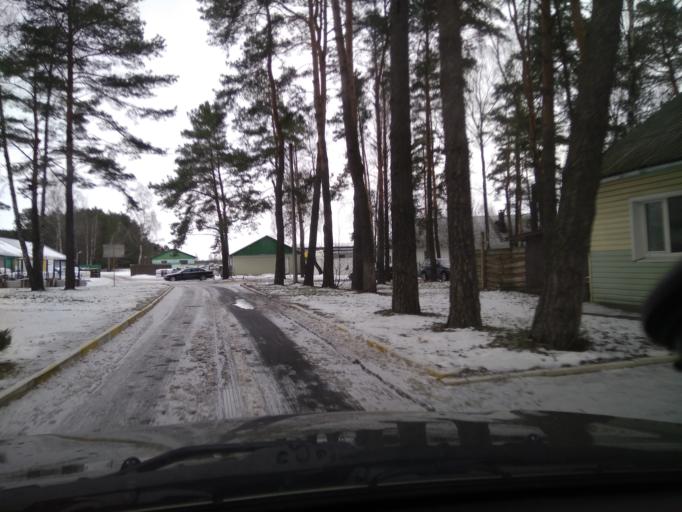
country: BY
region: Minsk
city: Borovlyany
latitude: 53.9609
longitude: 27.6504
